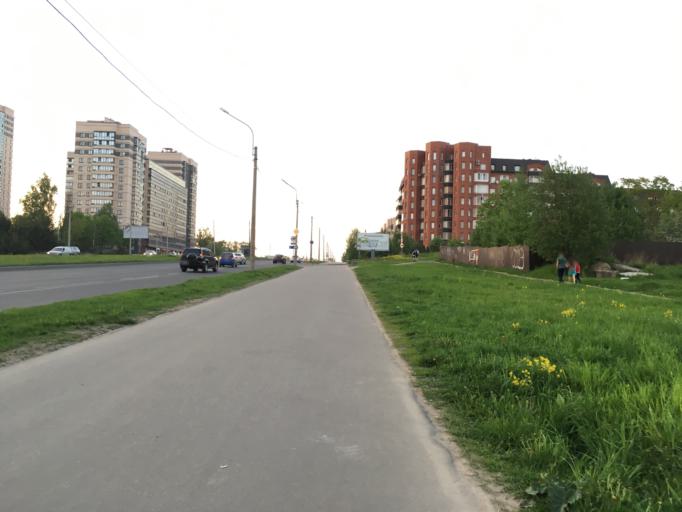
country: RU
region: St.-Petersburg
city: Kolomyagi
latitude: 60.0183
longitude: 30.2799
